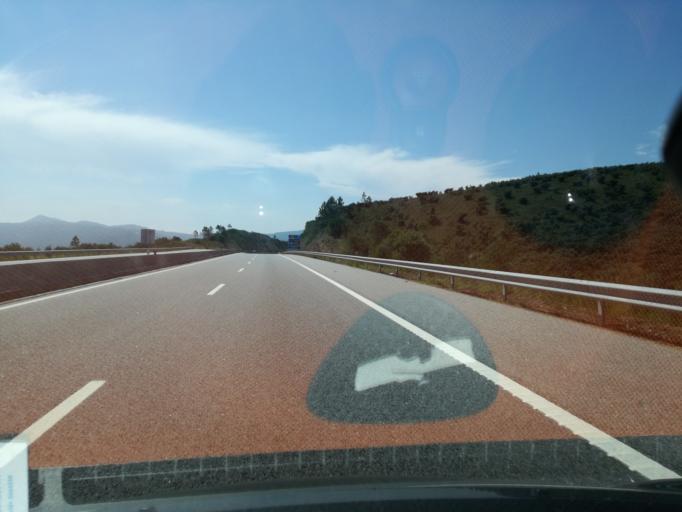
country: PT
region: Viana do Castelo
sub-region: Caminha
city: Vila Praia de Ancora
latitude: 41.8340
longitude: -8.7865
